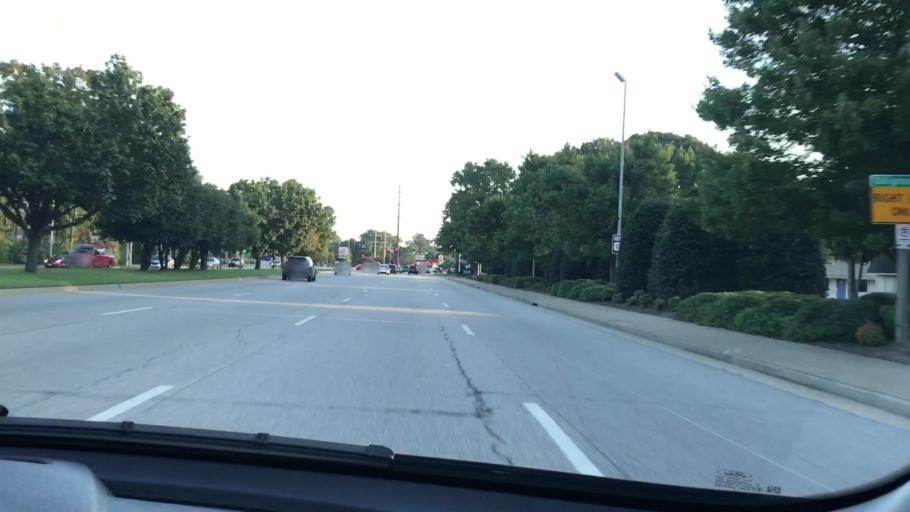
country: US
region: Virginia
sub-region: City of Newport News
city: Newport News
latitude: 37.0863
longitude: -76.4592
